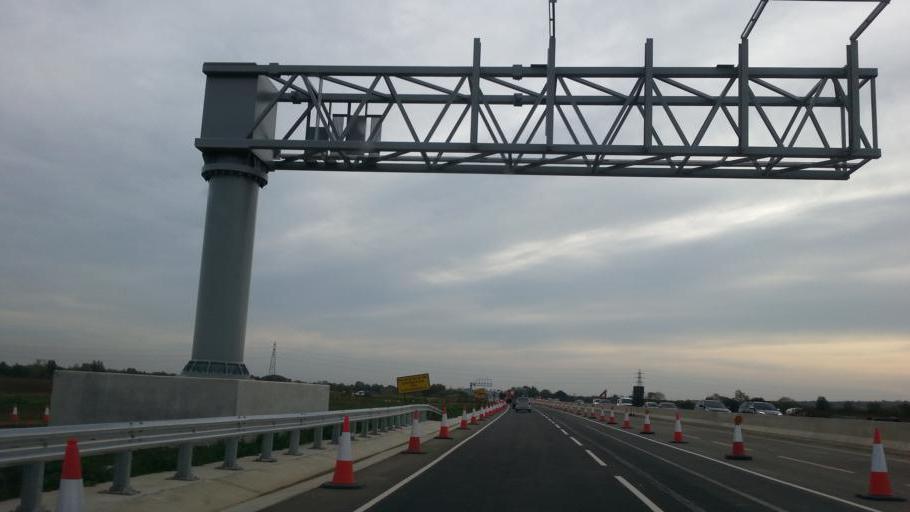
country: GB
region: England
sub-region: Cambridgeshire
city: Brampton
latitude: 52.3423
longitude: -0.2512
